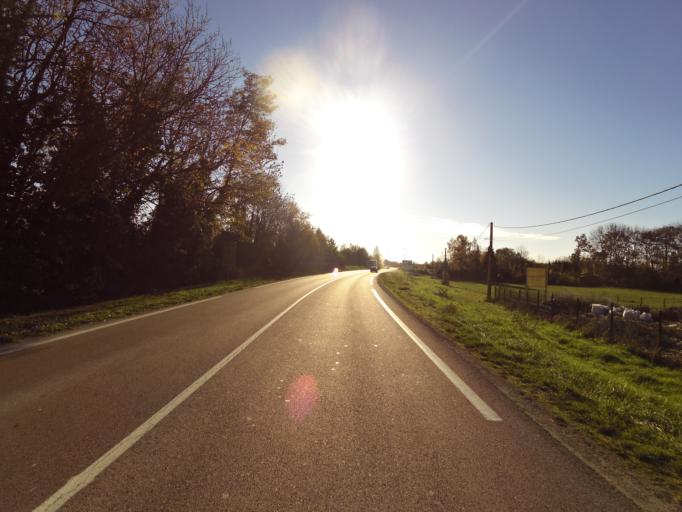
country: FR
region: Champagne-Ardenne
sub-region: Departement de l'Aube
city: Bucheres
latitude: 48.2289
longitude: 4.1294
